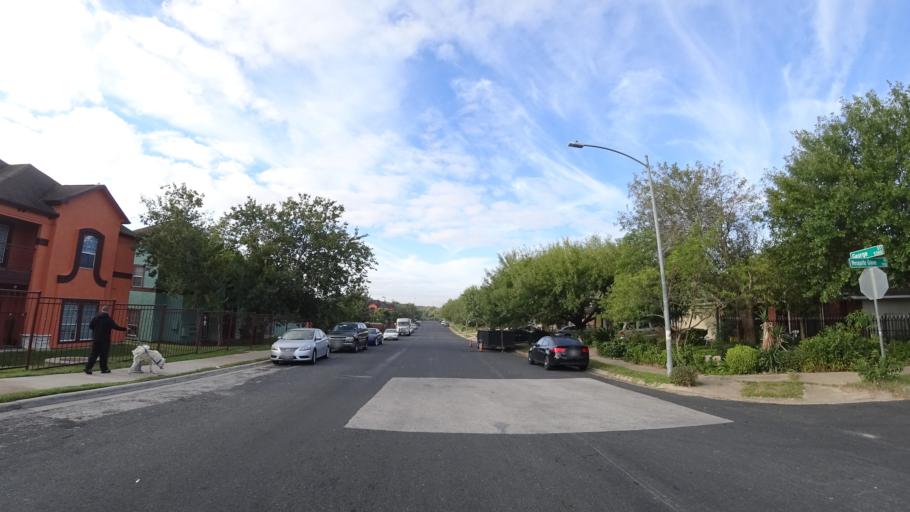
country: US
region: Texas
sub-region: Travis County
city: Onion Creek
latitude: 30.1904
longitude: -97.7344
